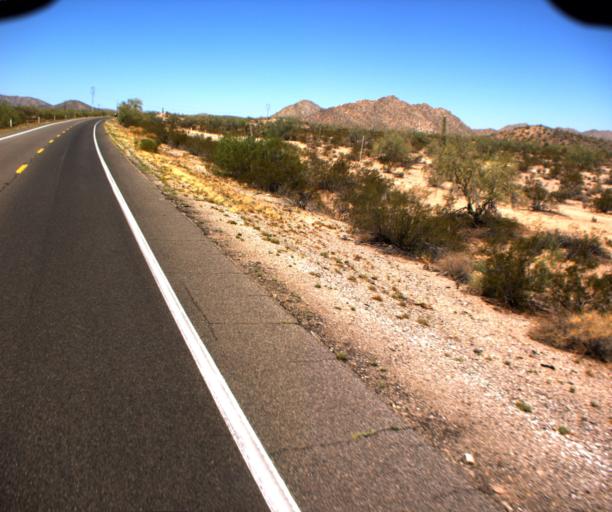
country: US
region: Arizona
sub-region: Pinal County
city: Maricopa
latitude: 32.8446
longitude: -112.0992
